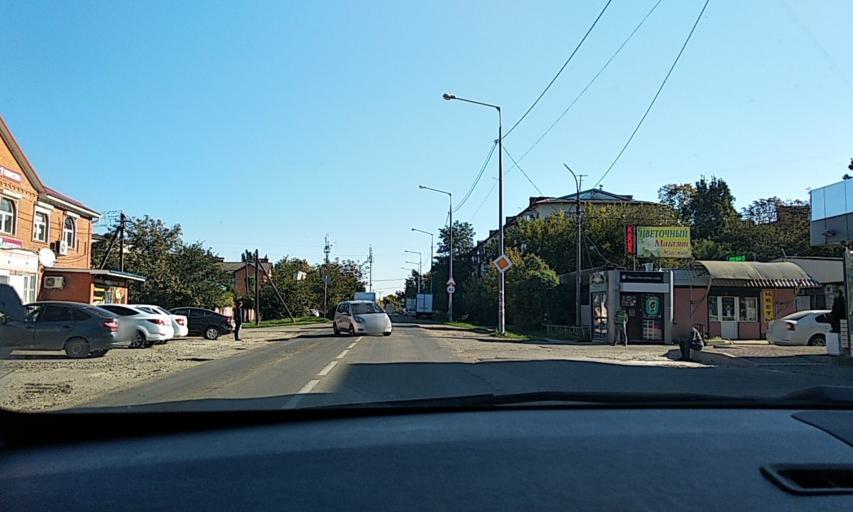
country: RU
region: Krasnodarskiy
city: Pashkovskiy
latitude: 45.0326
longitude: 39.1213
